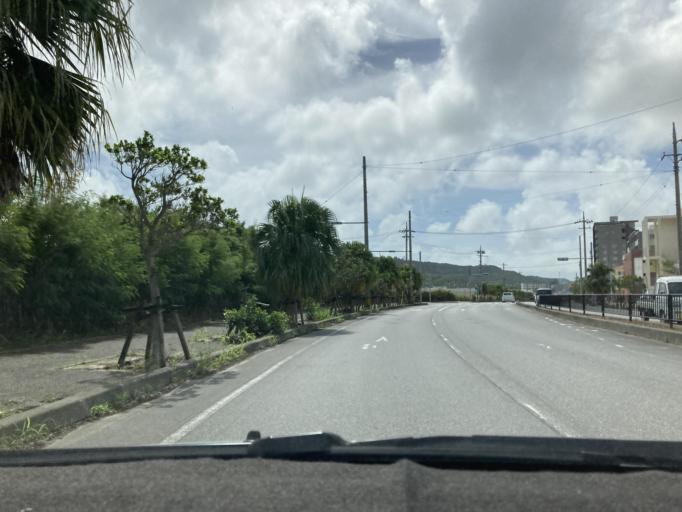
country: JP
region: Okinawa
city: Ginowan
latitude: 26.2101
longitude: 127.7645
